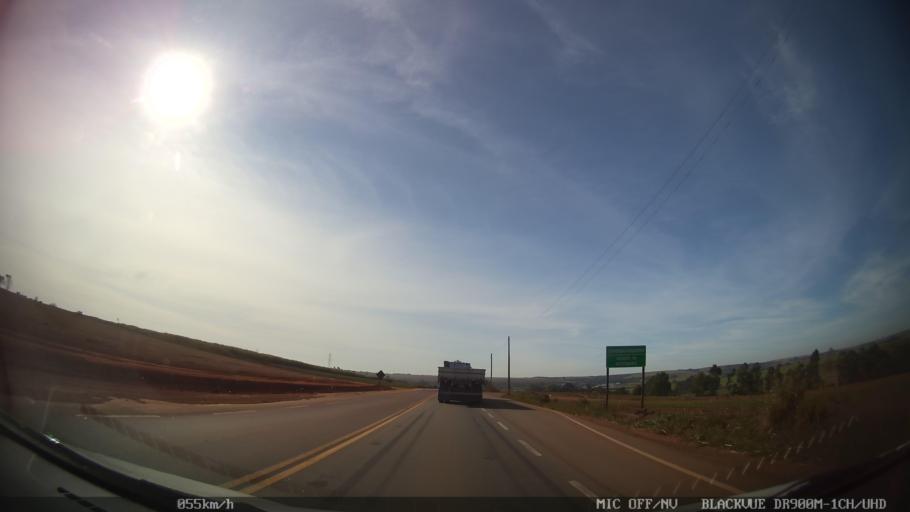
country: BR
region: Sao Paulo
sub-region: Piracicaba
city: Piracicaba
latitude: -22.7899
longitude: -47.6432
